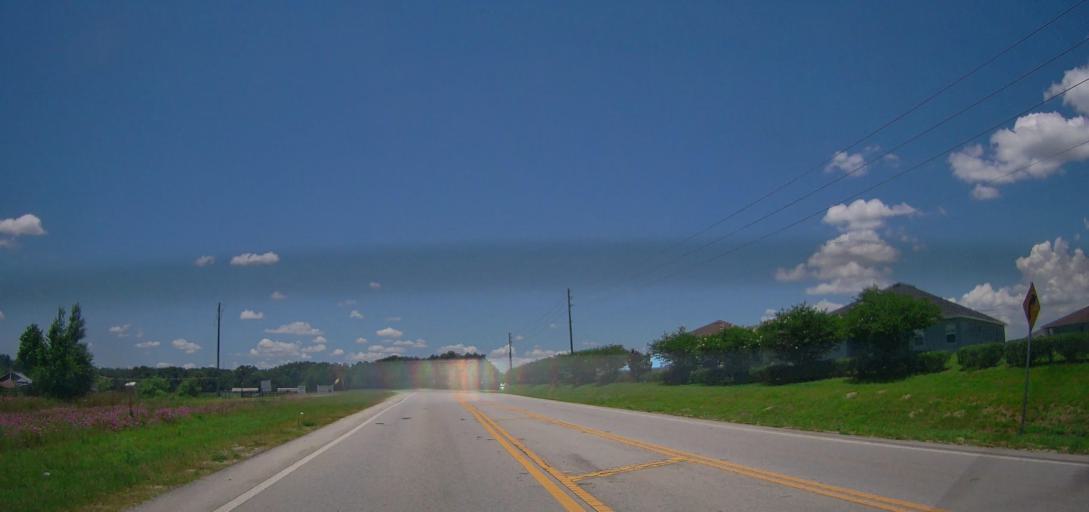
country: US
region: Florida
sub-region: Marion County
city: Belleview
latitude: 29.0864
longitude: -82.0652
